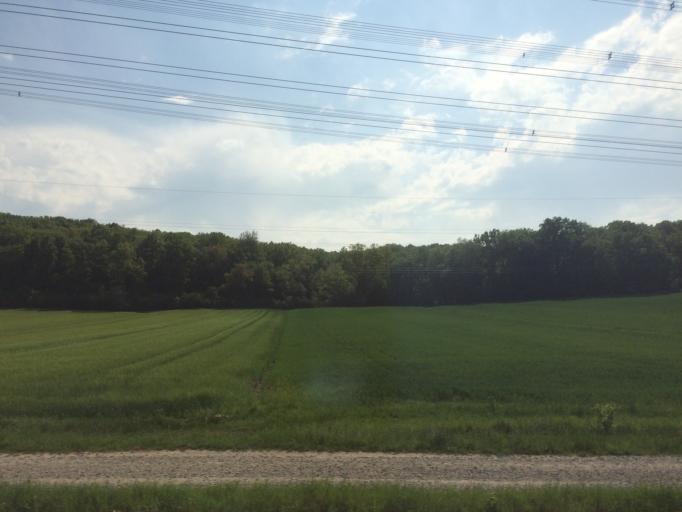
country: DE
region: Bavaria
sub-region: Regierungsbezirk Mittelfranken
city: Langenfeld
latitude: 49.6283
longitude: 10.4936
